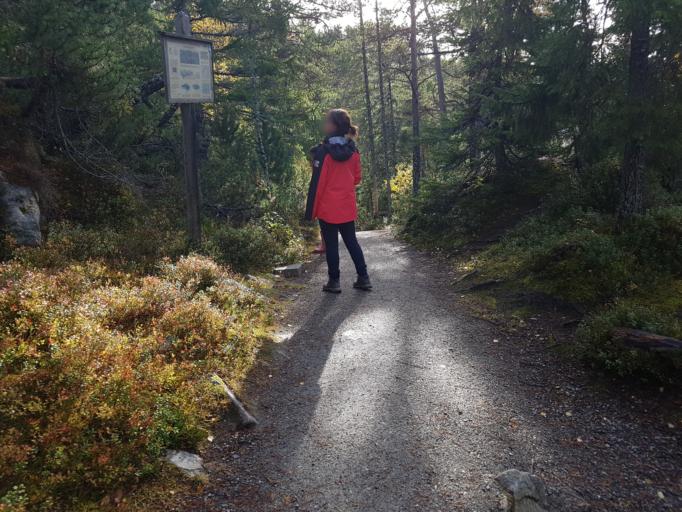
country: NO
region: Sor-Trondelag
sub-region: Trondheim
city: Trondheim
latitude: 63.4266
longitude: 10.2835
